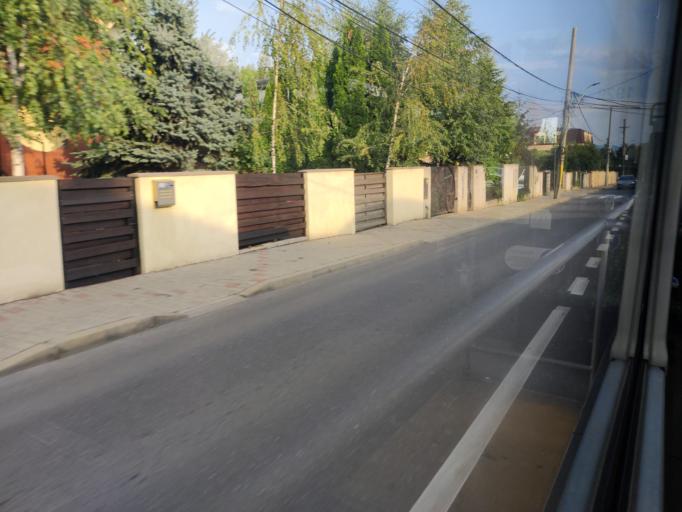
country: RO
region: Iasi
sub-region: Municipiul Iasi
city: Iasi
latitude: 47.1749
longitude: 27.5983
